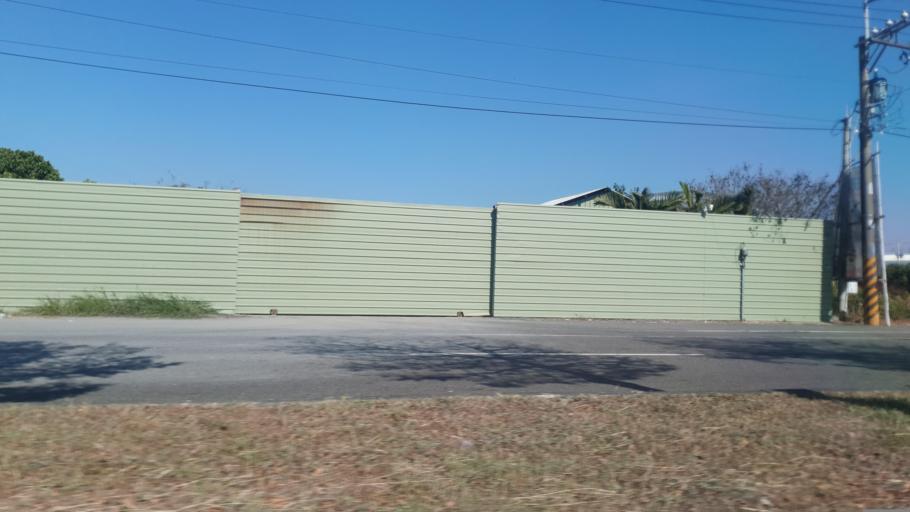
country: TW
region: Taiwan
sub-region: Tainan
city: Tainan
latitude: 23.0060
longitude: 120.2832
